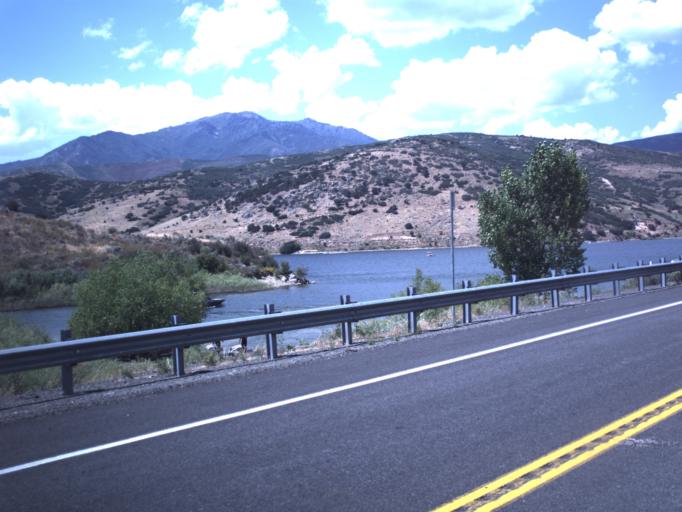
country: US
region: Utah
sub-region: Wasatch County
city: Midway
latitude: 40.4497
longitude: -111.4782
